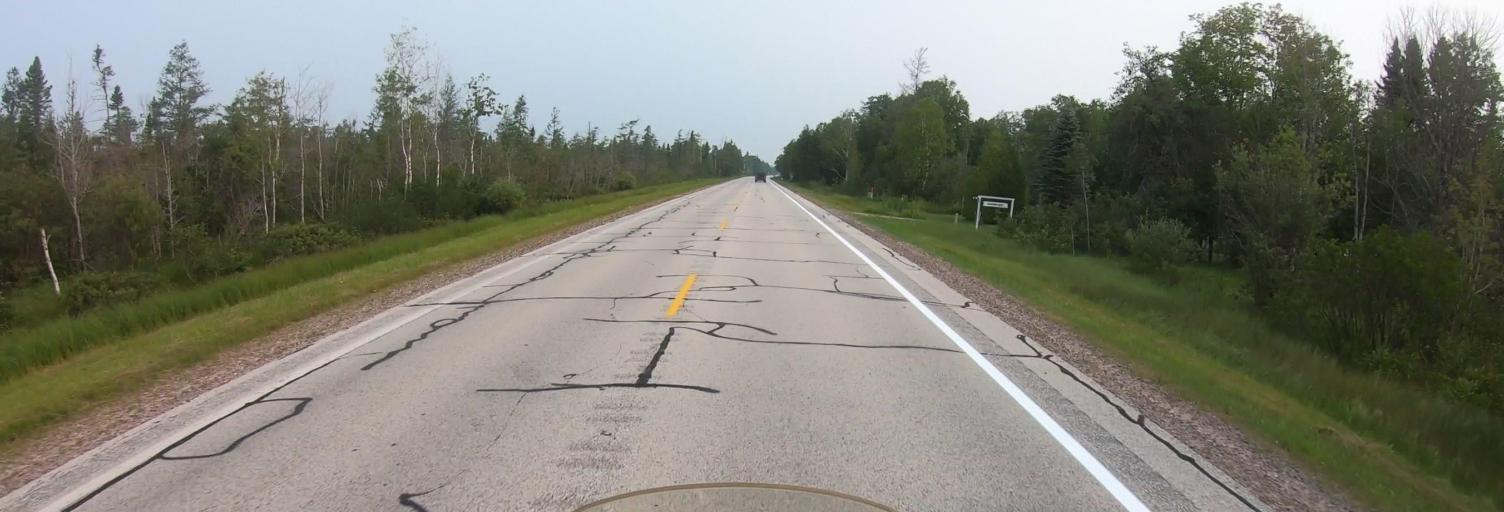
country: US
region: Michigan
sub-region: Luce County
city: Newberry
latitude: 46.5758
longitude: -85.0353
